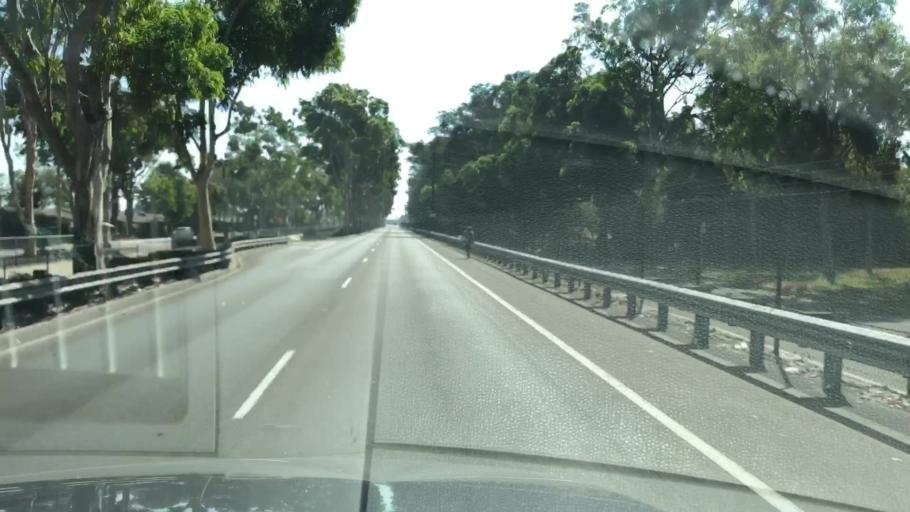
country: US
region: California
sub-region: Ventura County
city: Channel Islands Beach
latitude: 34.1757
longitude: -119.2033
